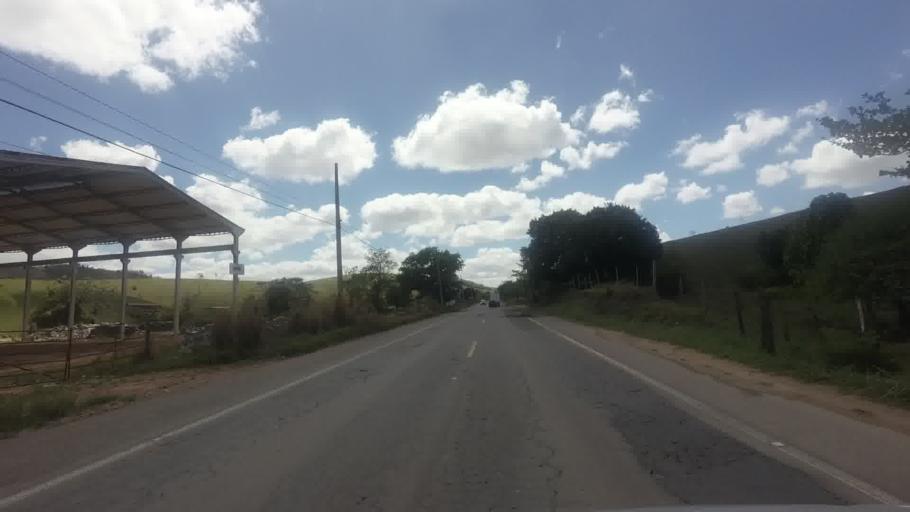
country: BR
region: Rio de Janeiro
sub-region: Santo Antonio De Padua
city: Santo Antonio de Padua
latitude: -21.6437
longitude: -42.2817
